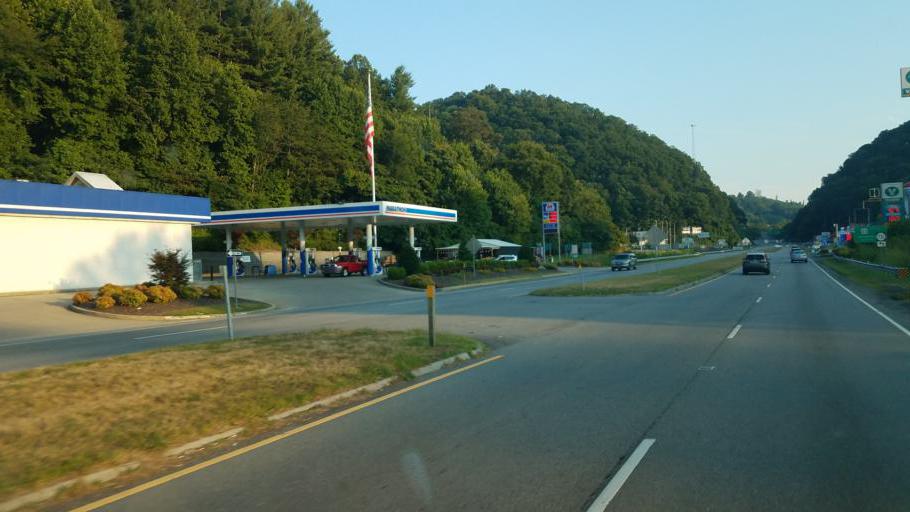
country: US
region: Virginia
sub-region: Scott County
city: Weber City
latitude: 36.6011
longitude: -82.5708
